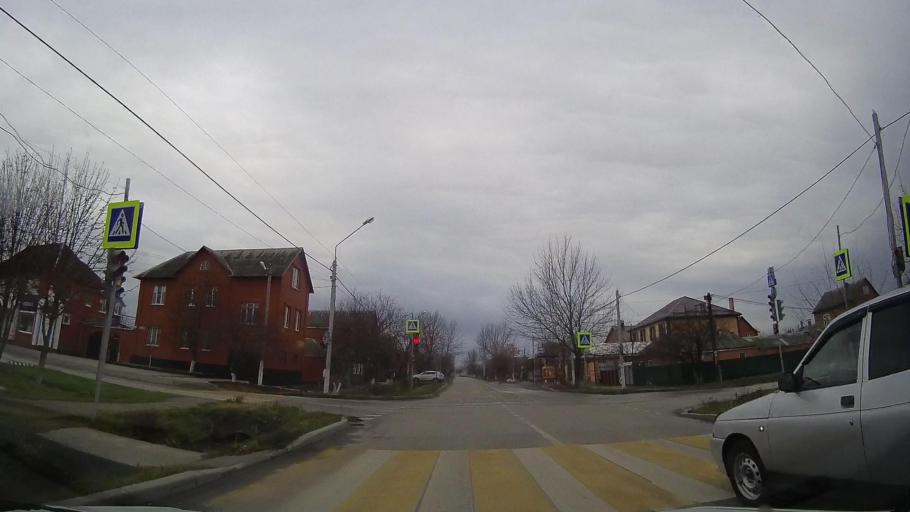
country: RU
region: Rostov
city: Bataysk
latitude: 47.1209
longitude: 39.7435
